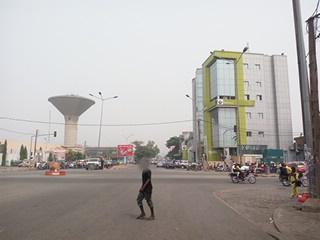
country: BJ
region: Littoral
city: Cotonou
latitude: 6.3590
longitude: 2.4194
